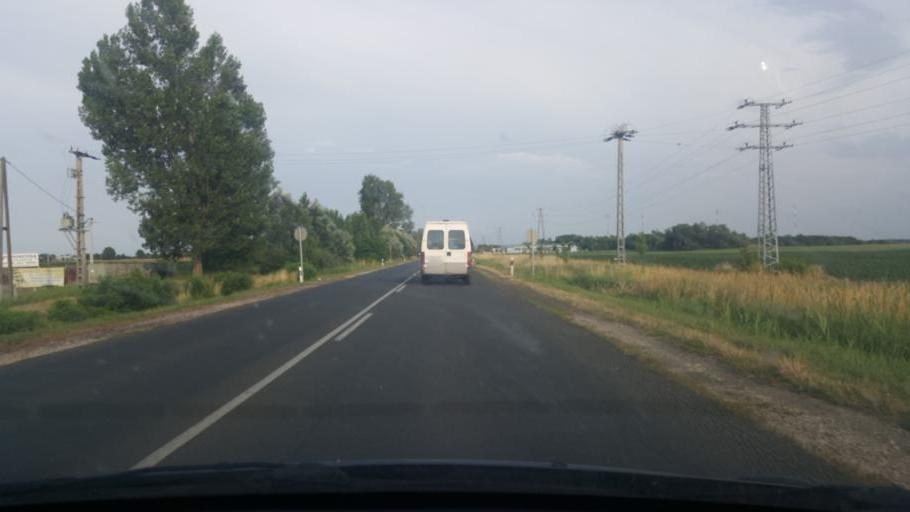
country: HU
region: Pest
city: Peteri
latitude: 47.3531
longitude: 19.4037
